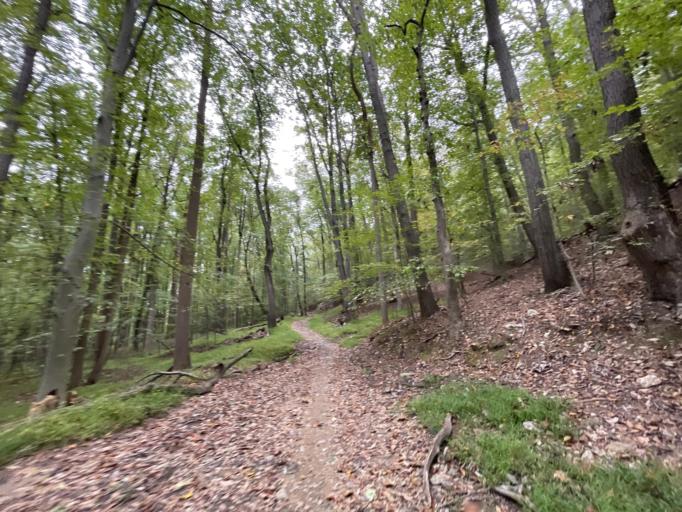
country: US
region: Maryland
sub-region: Baltimore County
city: Hampton
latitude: 39.4334
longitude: -76.5697
